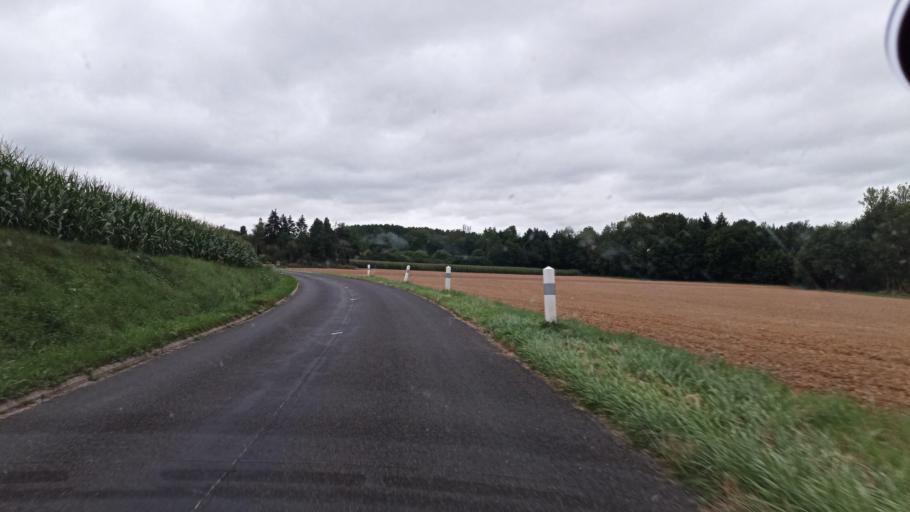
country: FR
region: Ile-de-France
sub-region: Departement de Seine-et-Marne
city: Voulx
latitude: 48.2632
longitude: 3.0117
